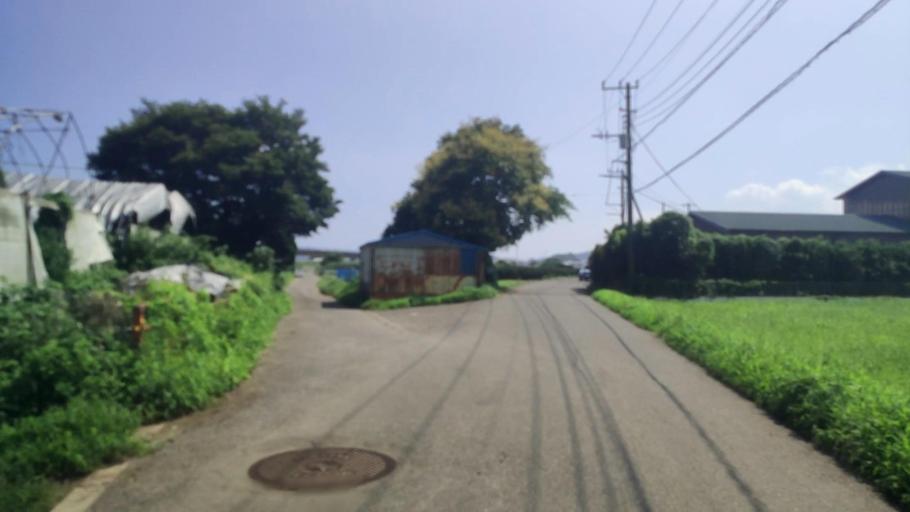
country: JP
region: Kanagawa
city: Isehara
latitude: 35.3678
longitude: 139.3072
